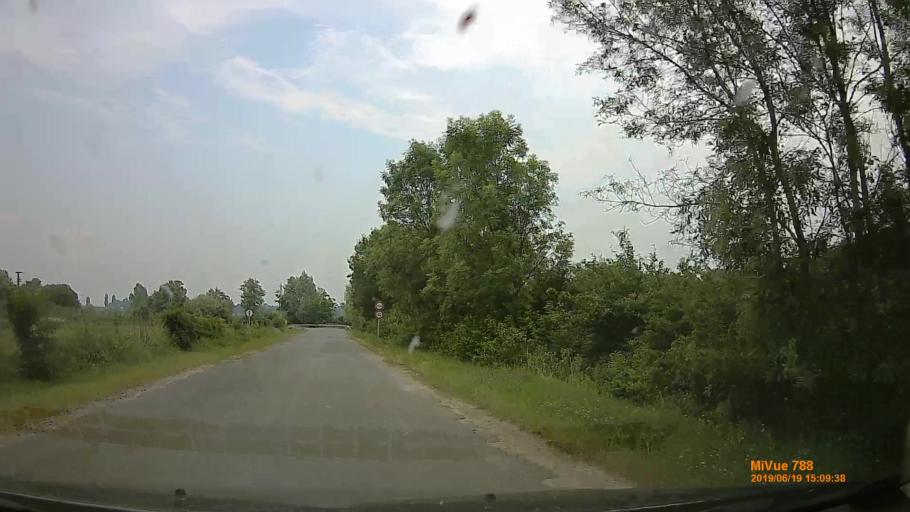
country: HU
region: Baranya
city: Szigetvar
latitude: 46.0830
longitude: 17.8051
